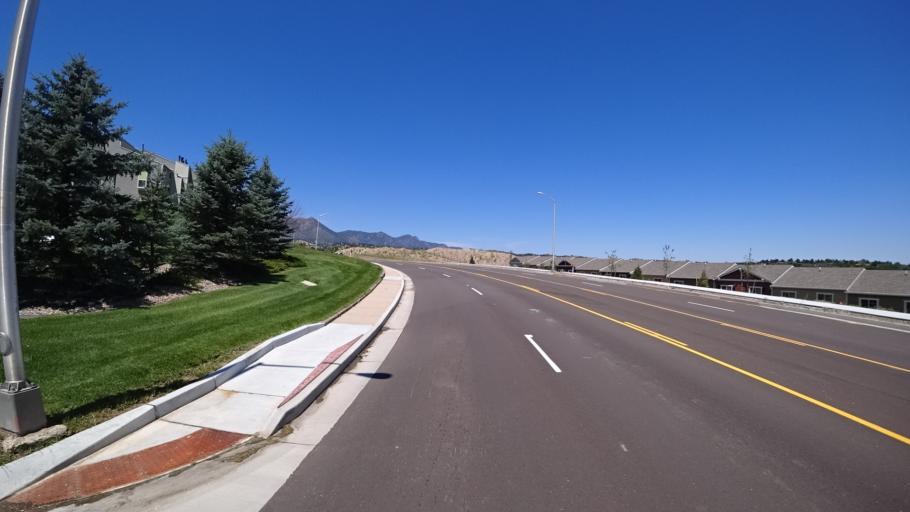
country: US
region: Colorado
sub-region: El Paso County
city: Colorado Springs
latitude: 38.9165
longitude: -104.8316
